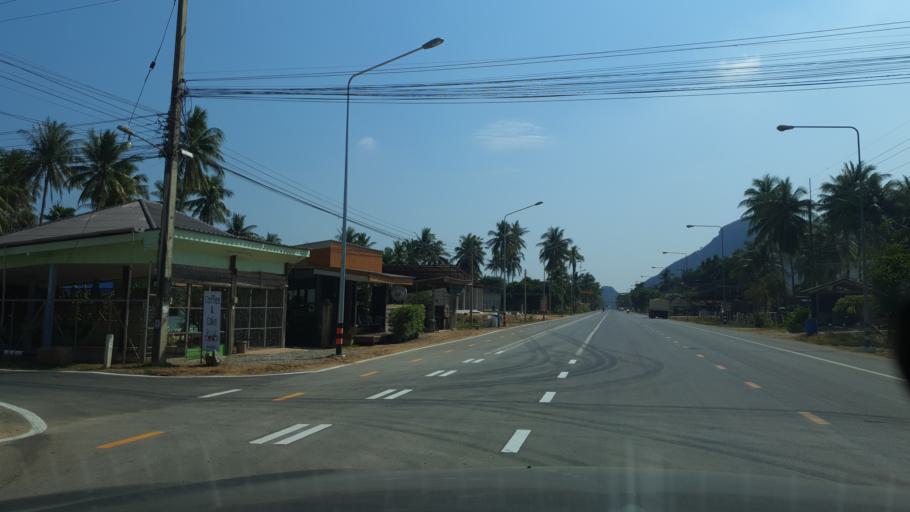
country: TH
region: Prachuap Khiri Khan
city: Sam Roi Yot
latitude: 12.2382
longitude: 99.9665
